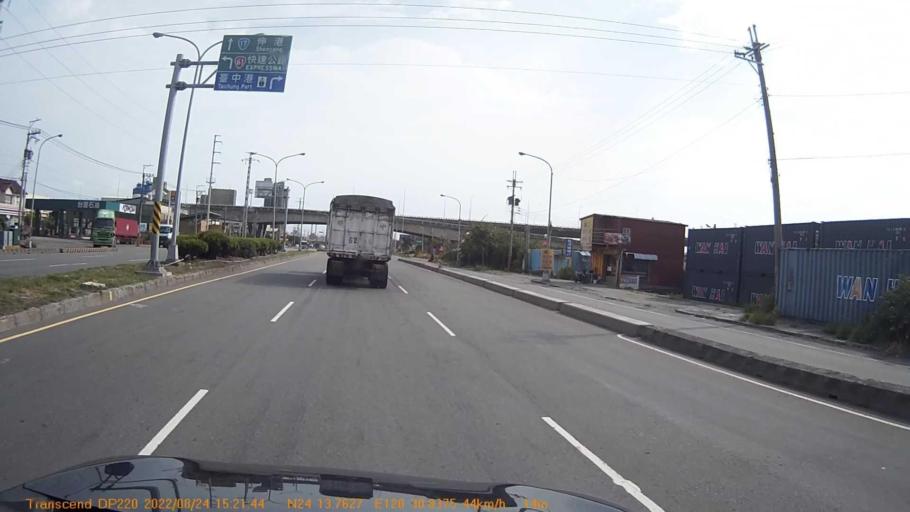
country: TW
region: Taiwan
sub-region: Changhua
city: Chang-hua
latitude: 24.2290
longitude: 120.5138
